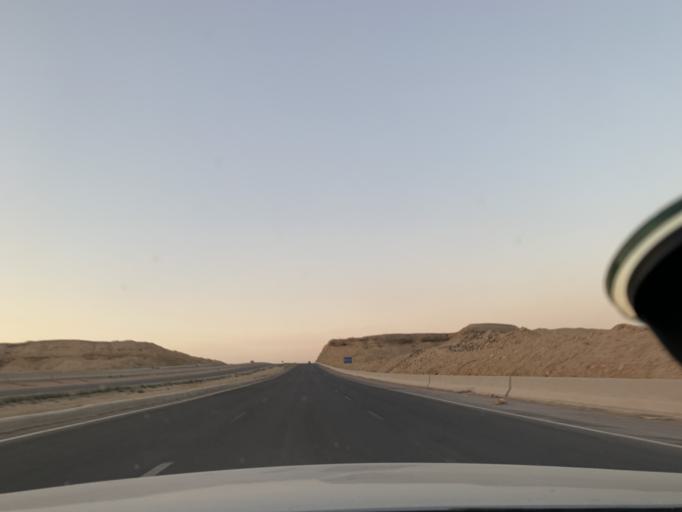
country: EG
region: Muhafazat al Qahirah
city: Halwan
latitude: 29.9467
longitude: 31.5357
